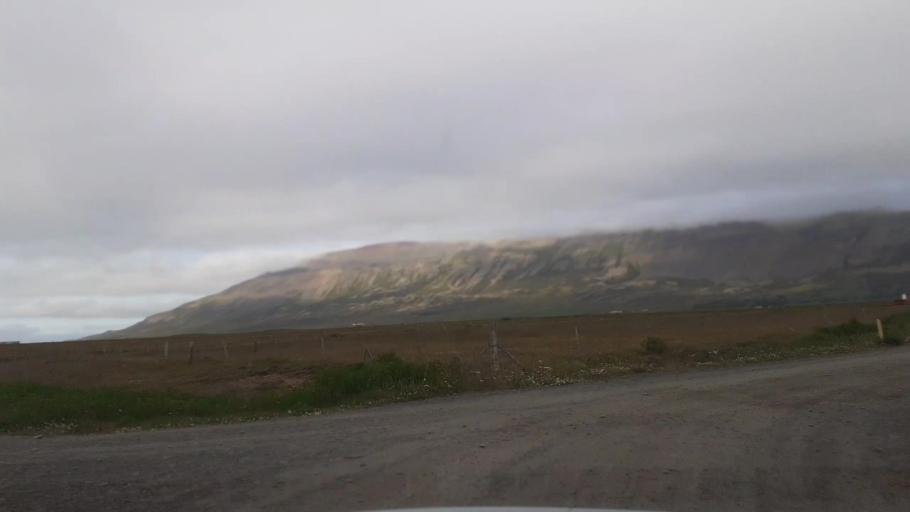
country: IS
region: Northwest
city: Saudarkrokur
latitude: 65.9028
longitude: -19.4209
